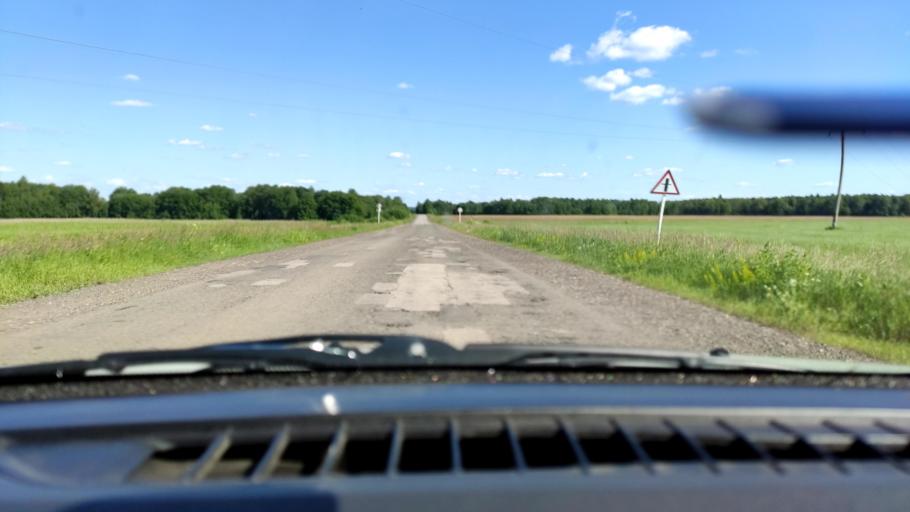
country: RU
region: Perm
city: Uinskoye
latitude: 57.2321
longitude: 56.5467
